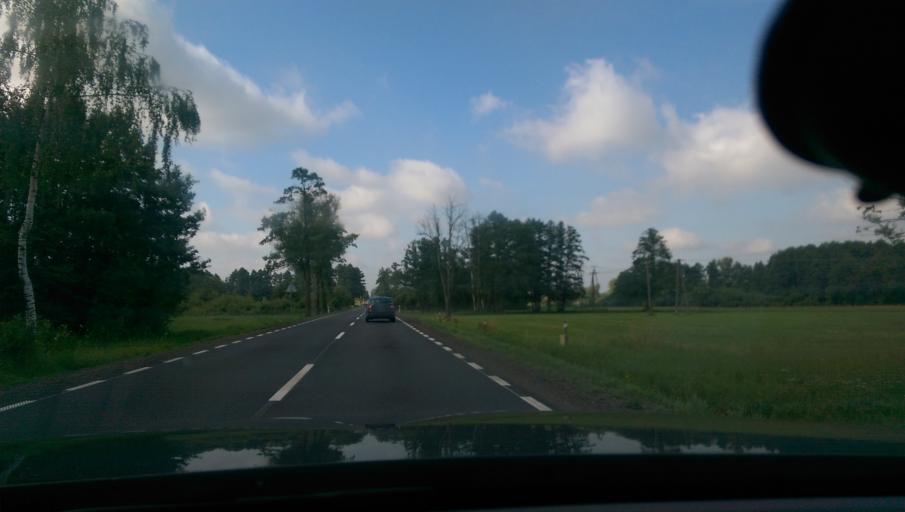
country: PL
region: Masovian Voivodeship
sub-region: Powiat plonski
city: Sochocin
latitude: 52.7245
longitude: 20.5084
